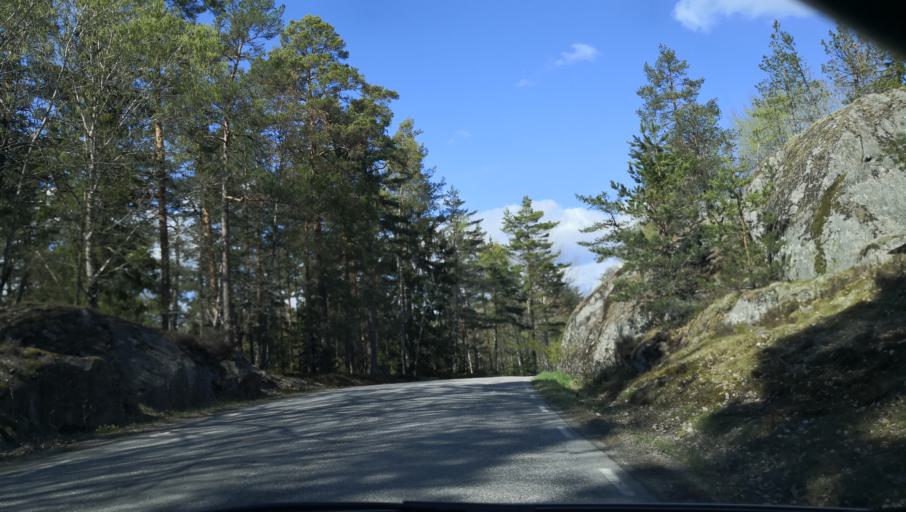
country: SE
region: Stockholm
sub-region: Varmdo Kommun
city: Hemmesta
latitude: 59.3972
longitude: 18.5102
